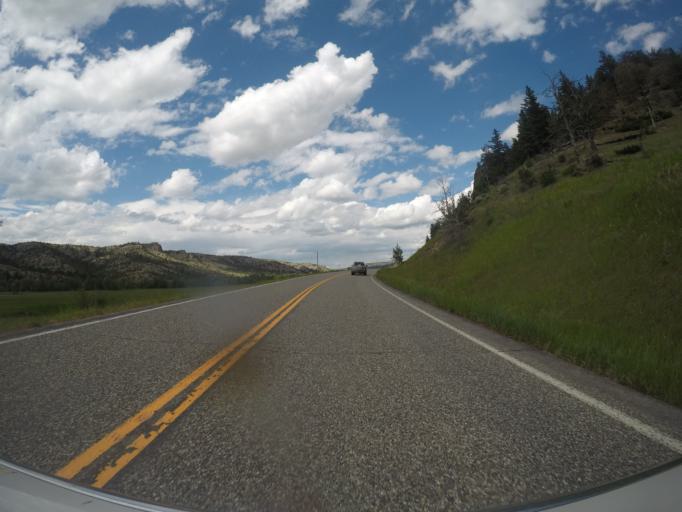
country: US
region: Montana
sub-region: Sweet Grass County
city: Big Timber
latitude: 45.7000
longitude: -110.0183
